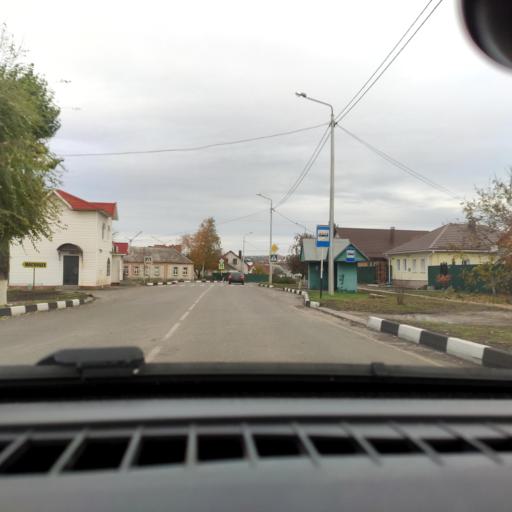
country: RU
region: Belgorod
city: Alekseyevka
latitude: 50.6335
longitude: 38.7004
